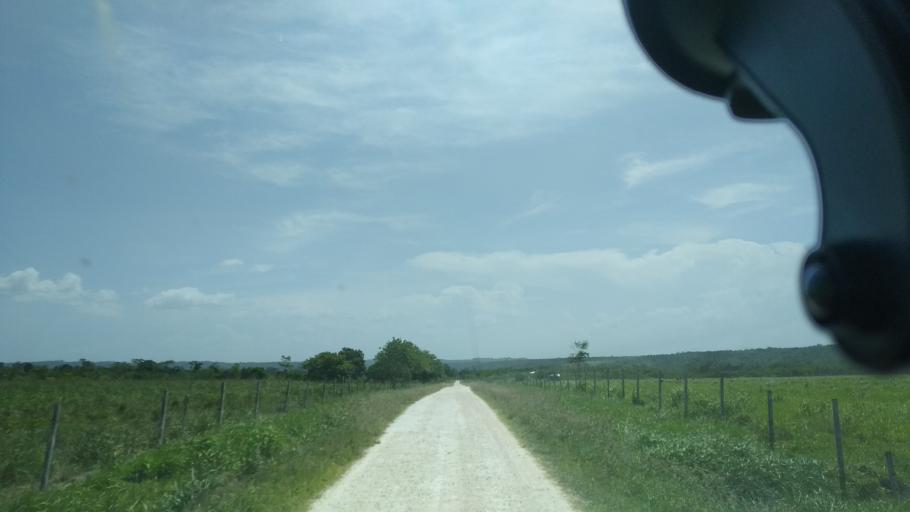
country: BZ
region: Cayo
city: San Ignacio
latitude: 17.2891
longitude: -89.0770
